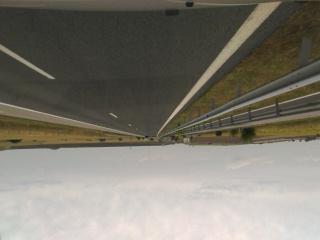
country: BG
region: Stara Zagora
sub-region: Obshtina Chirpan
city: Chirpan
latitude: 42.1976
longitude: 25.2657
